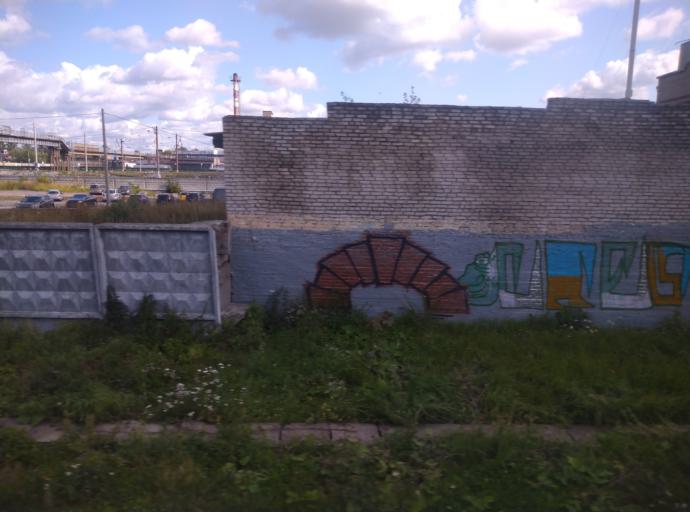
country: RU
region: St.-Petersburg
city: Obukhovo
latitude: 59.8774
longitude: 30.4099
